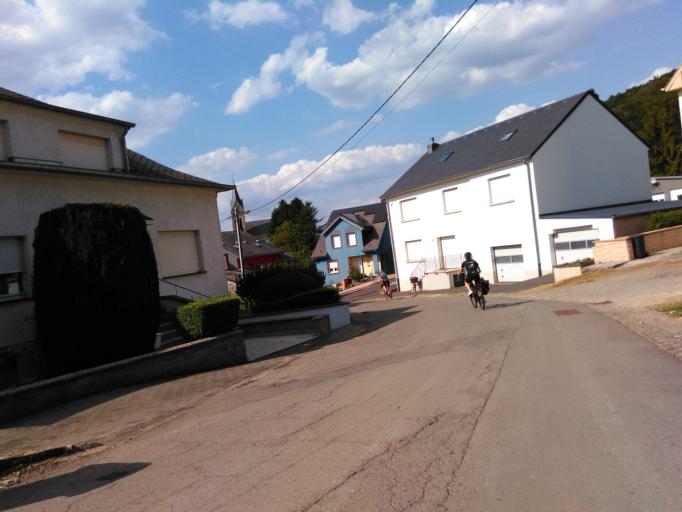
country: LU
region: Luxembourg
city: Tetange
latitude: 49.4724
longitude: 6.0407
